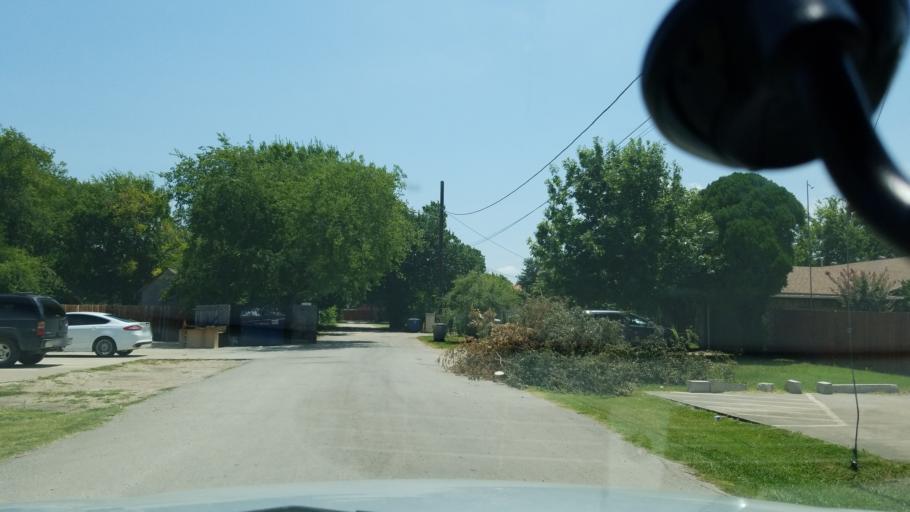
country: US
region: Texas
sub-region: Dallas County
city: Cockrell Hill
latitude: 32.7194
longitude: -96.8653
